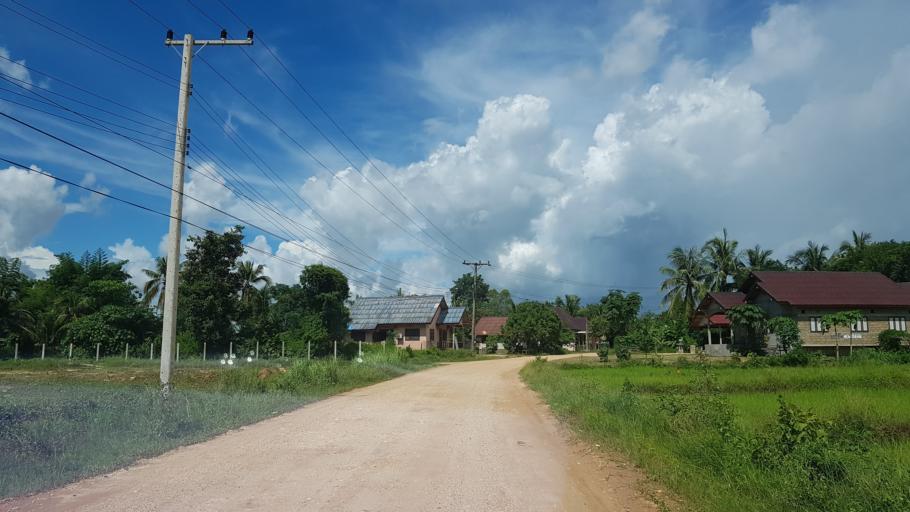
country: LA
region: Vientiane
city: Vientiane
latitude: 18.2163
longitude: 102.5111
